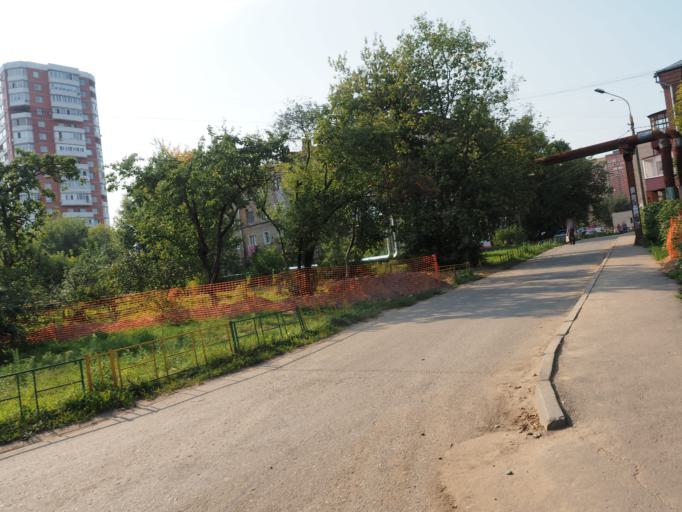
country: RU
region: Moskovskaya
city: Oktyabr'skiy
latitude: 55.6070
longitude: 37.9730
